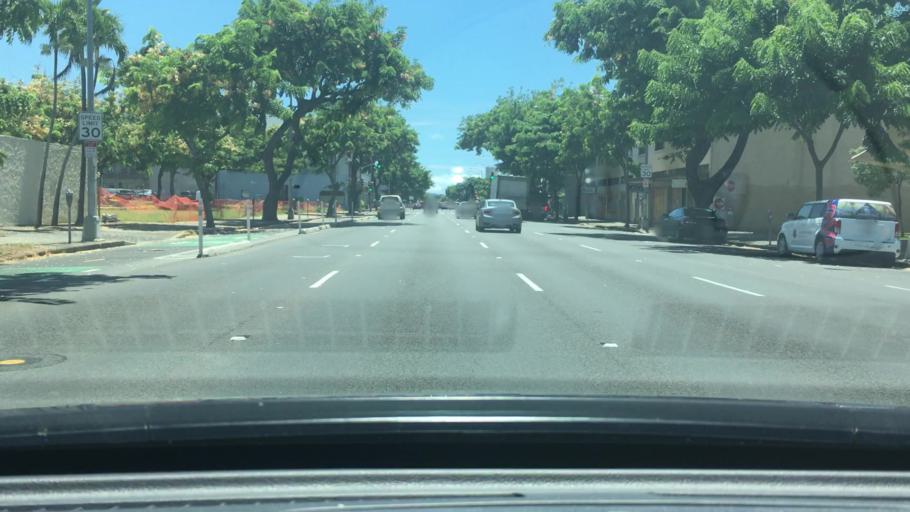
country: US
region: Hawaii
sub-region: Honolulu County
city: Honolulu
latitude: 21.2981
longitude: -157.8392
